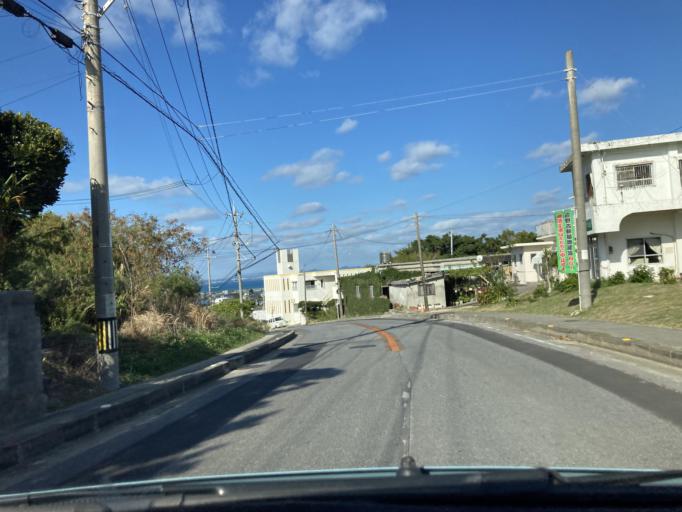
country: JP
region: Okinawa
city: Katsuren-haebaru
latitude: 26.3187
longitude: 127.9093
